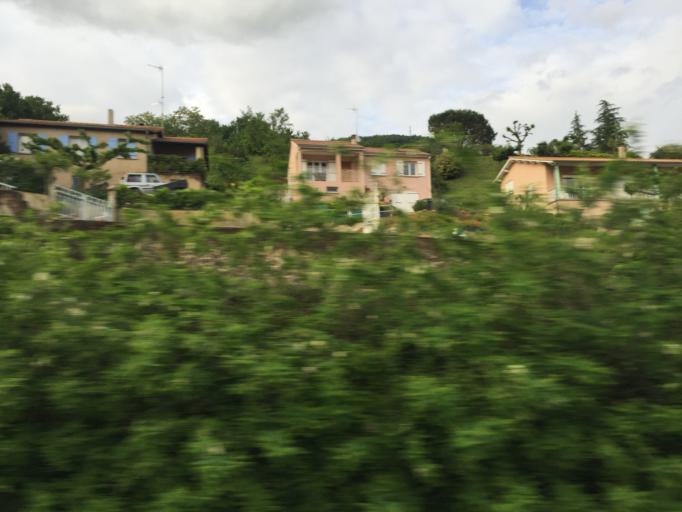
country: FR
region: Rhone-Alpes
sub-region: Departement de la Drome
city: Saint-Vallier
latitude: 45.1624
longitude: 4.8287
